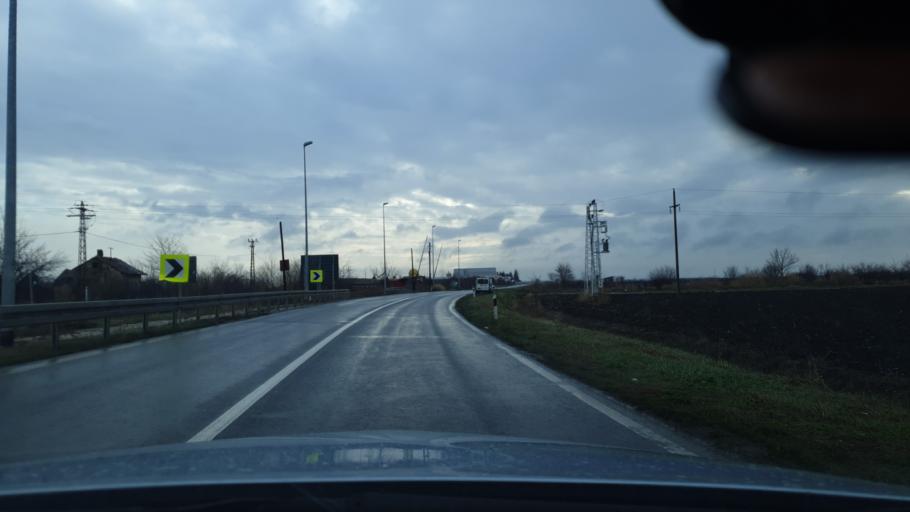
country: RS
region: Autonomna Pokrajina Vojvodina
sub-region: Juznobanatski Okrug
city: Kovin
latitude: 44.8095
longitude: 20.8898
